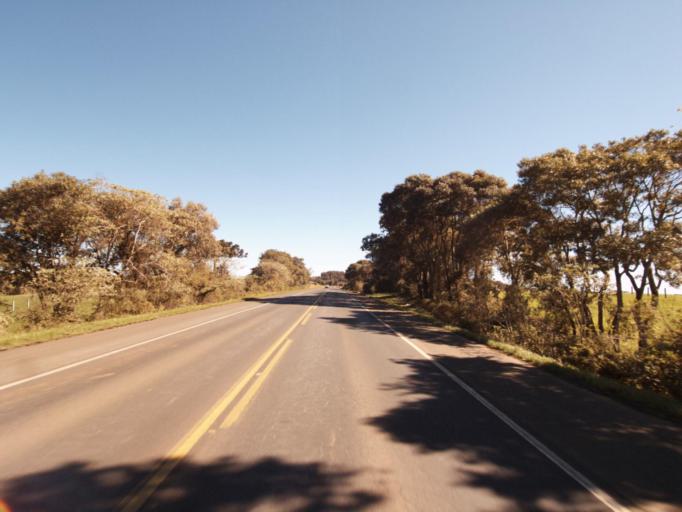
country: BR
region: Santa Catarina
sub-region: Xanxere
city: Xanxere
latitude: -26.8618
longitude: -52.2294
